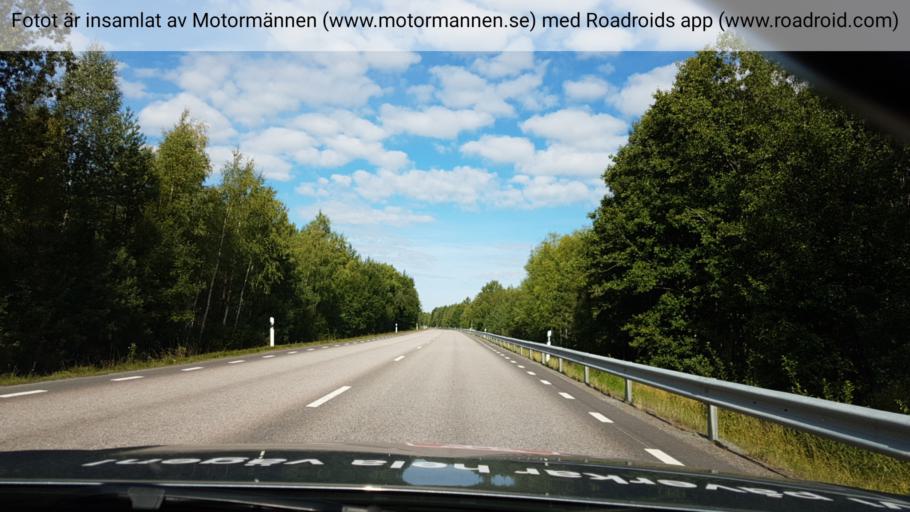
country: SE
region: Uppsala
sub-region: Osthammars Kommun
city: Bjorklinge
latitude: 59.9633
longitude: 17.3889
